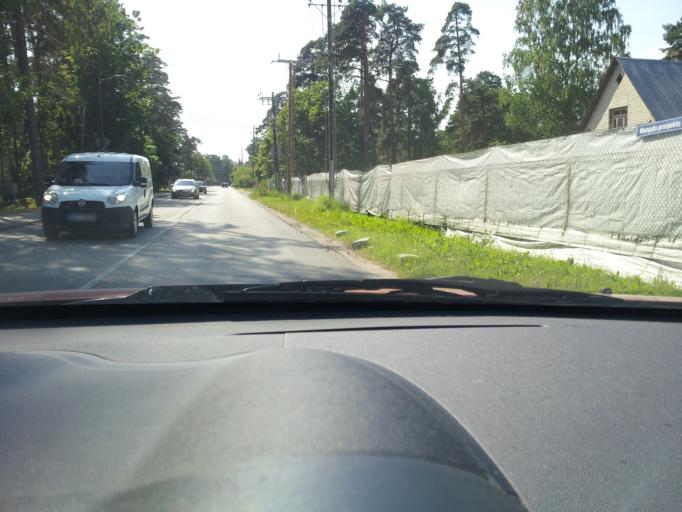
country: LV
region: Riga
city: Bolderaja
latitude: 57.0708
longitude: 24.1048
